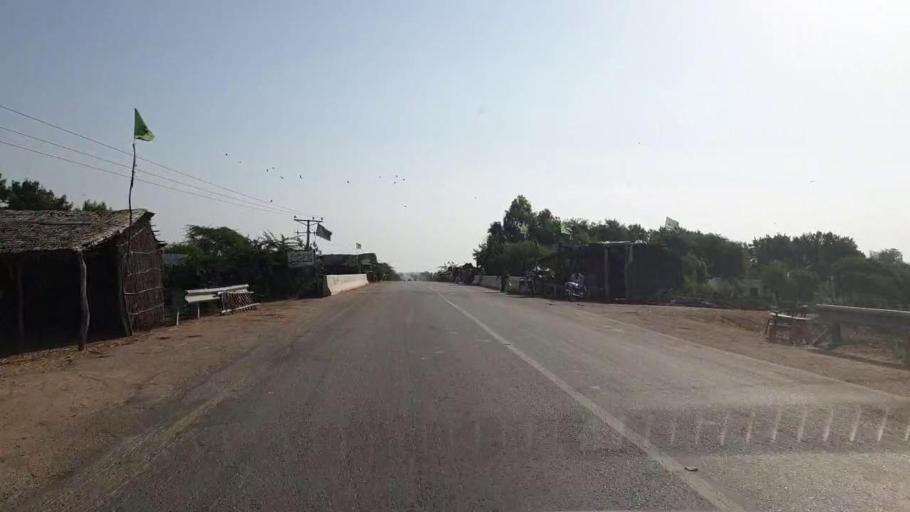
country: PK
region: Sindh
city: Tando Bago
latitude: 24.6578
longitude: 68.9783
